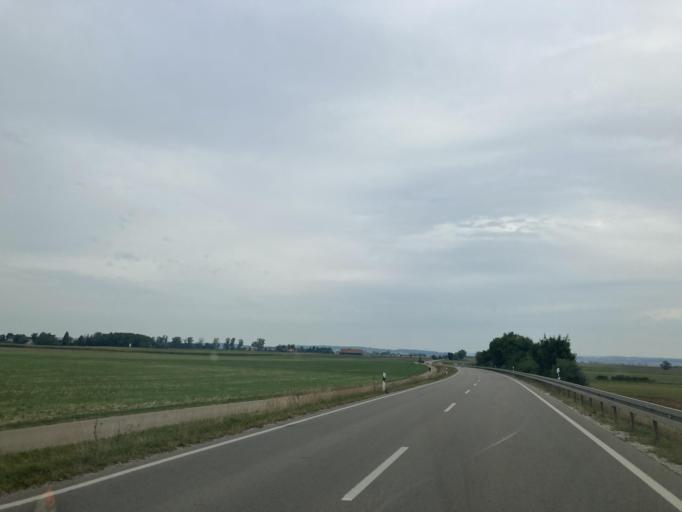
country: DE
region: Bavaria
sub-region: Swabia
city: Deiningen
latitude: 48.9018
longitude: 10.5591
